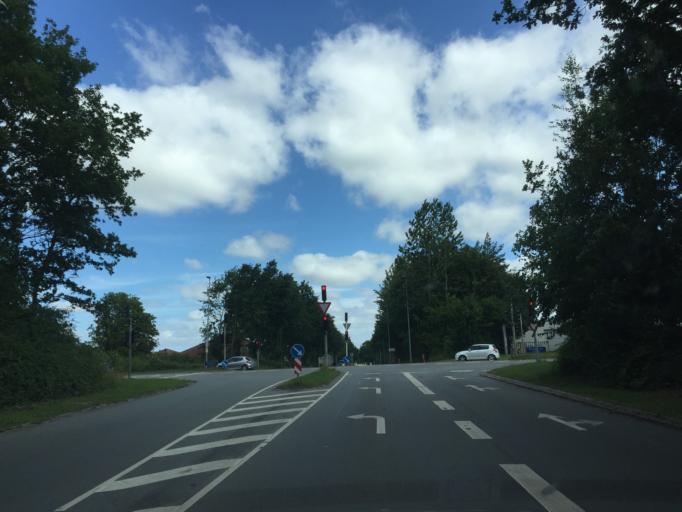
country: DK
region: South Denmark
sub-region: Odense Kommune
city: Neder Holluf
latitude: 55.3671
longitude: 10.4535
